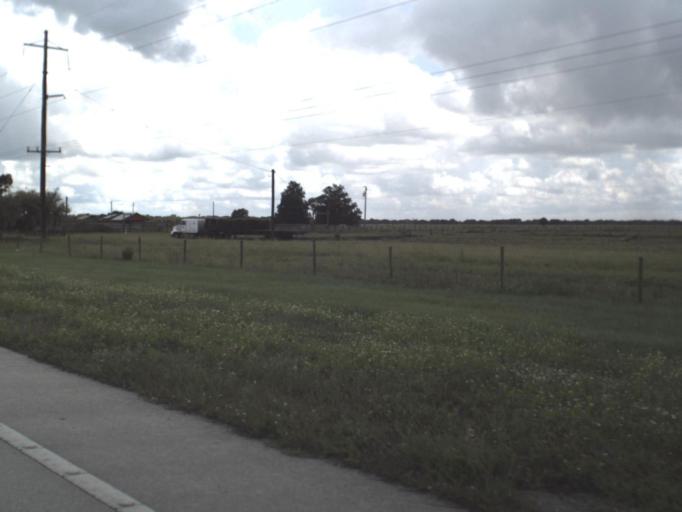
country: US
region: Florida
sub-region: DeSoto County
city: Southeast Arcadia
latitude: 27.2095
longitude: -81.6956
